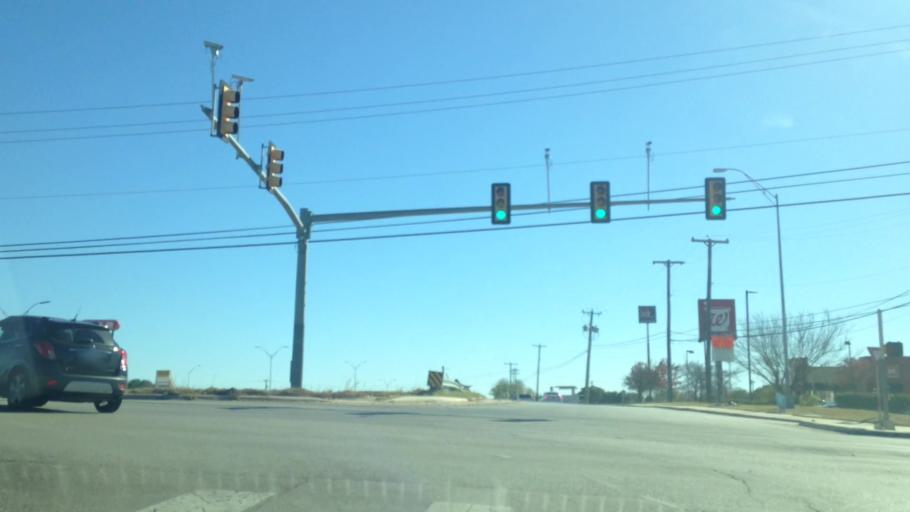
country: US
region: Texas
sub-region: Bexar County
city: Lackland Air Force Base
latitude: 29.3804
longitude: -98.6421
